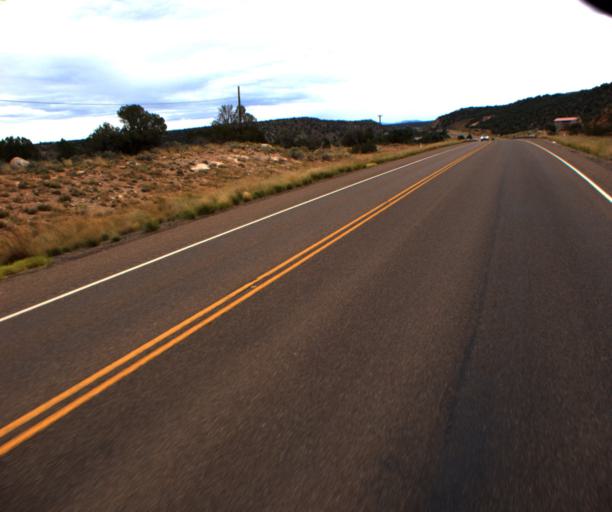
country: US
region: Arizona
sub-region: Navajo County
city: Taylor
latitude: 34.4113
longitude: -110.0808
